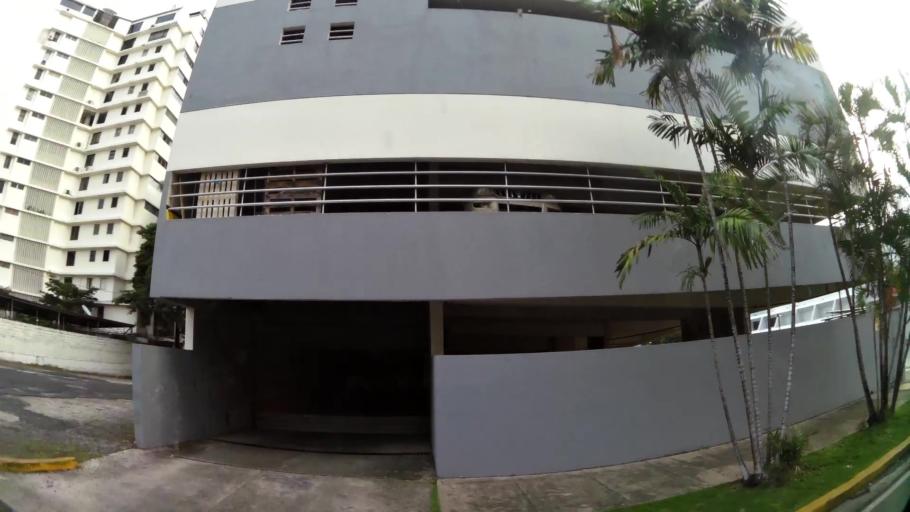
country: PA
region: Panama
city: Panama
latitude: 8.9908
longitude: -79.4982
